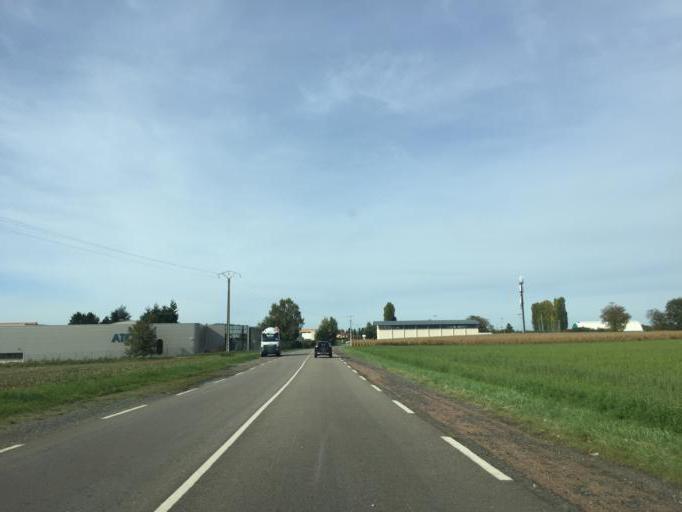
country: FR
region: Rhone-Alpes
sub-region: Departement du Rhone
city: Montanay
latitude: 45.8825
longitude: 4.8781
